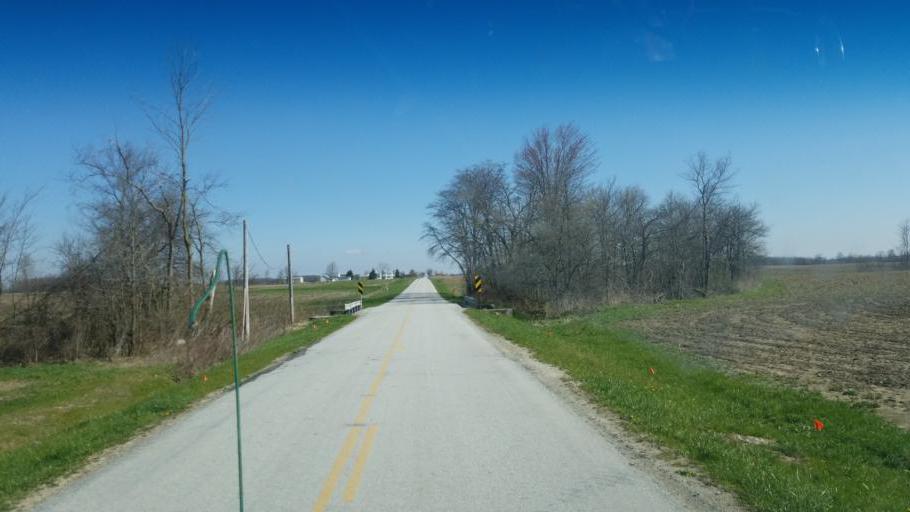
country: US
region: Ohio
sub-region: Hardin County
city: Forest
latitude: 40.7016
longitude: -83.4958
